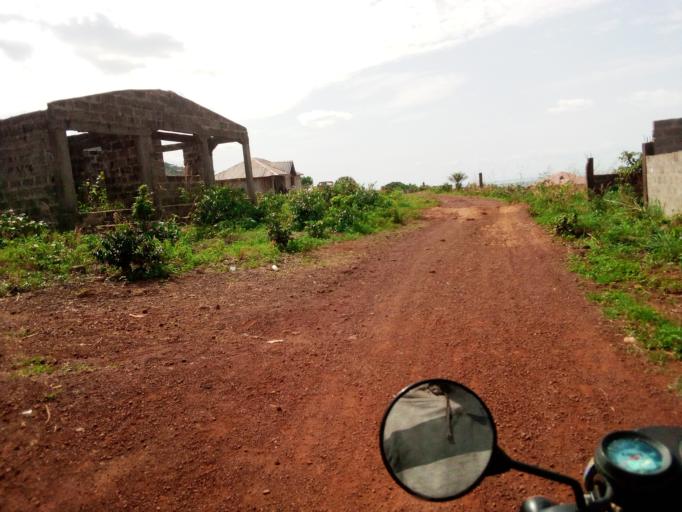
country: SL
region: Western Area
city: Waterloo
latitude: 8.3431
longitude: -13.0813
